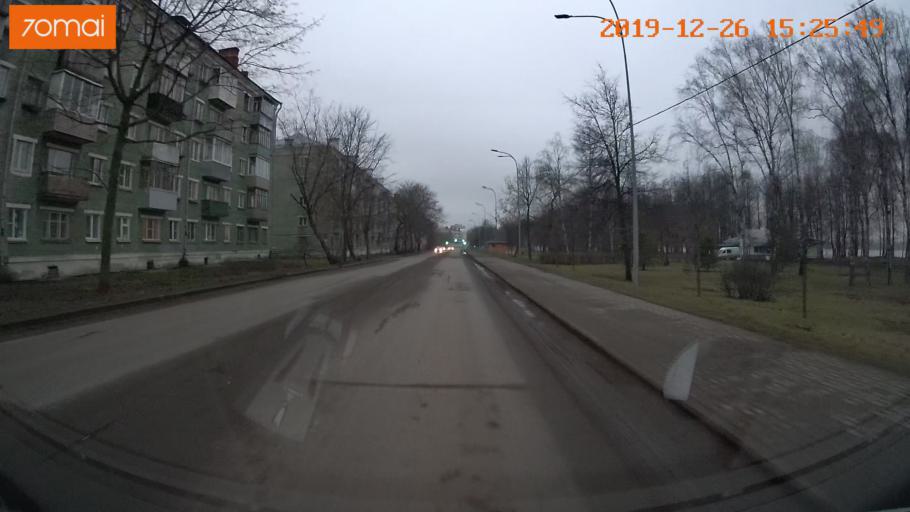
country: RU
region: Jaroslavl
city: Rybinsk
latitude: 58.0547
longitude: 38.8350
